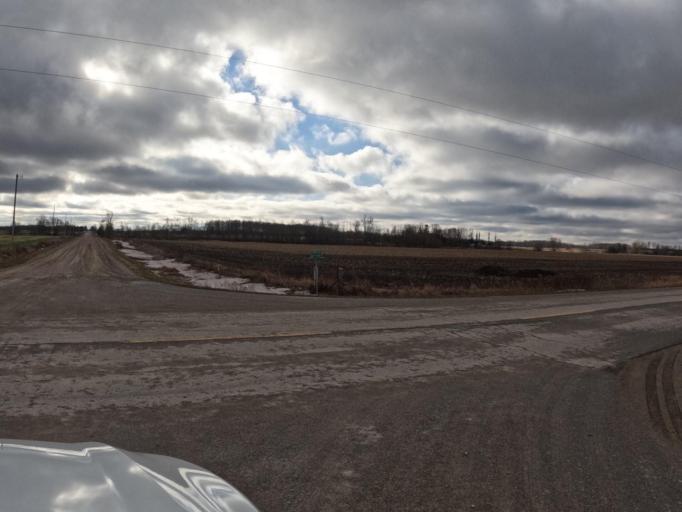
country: CA
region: Ontario
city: Shelburne
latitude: 43.9866
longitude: -80.3838
